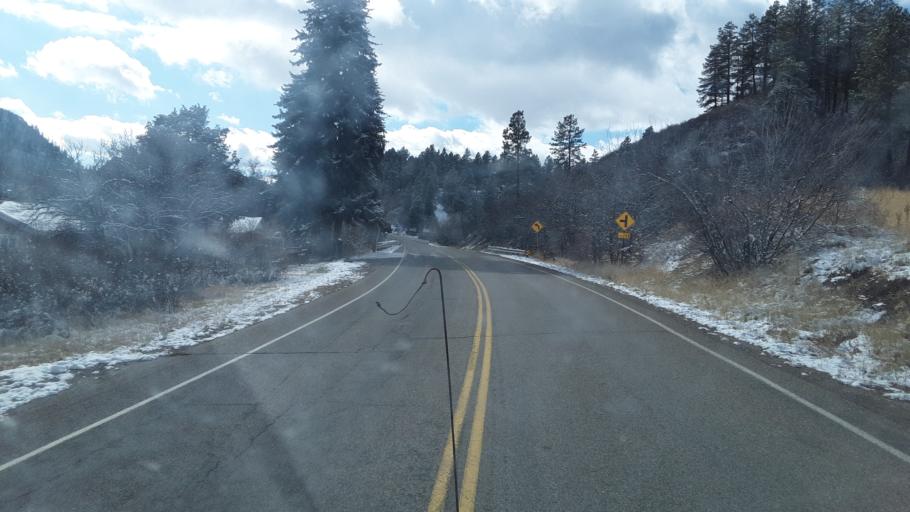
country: US
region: Colorado
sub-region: La Plata County
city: Durango
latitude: 37.3214
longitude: -107.7677
